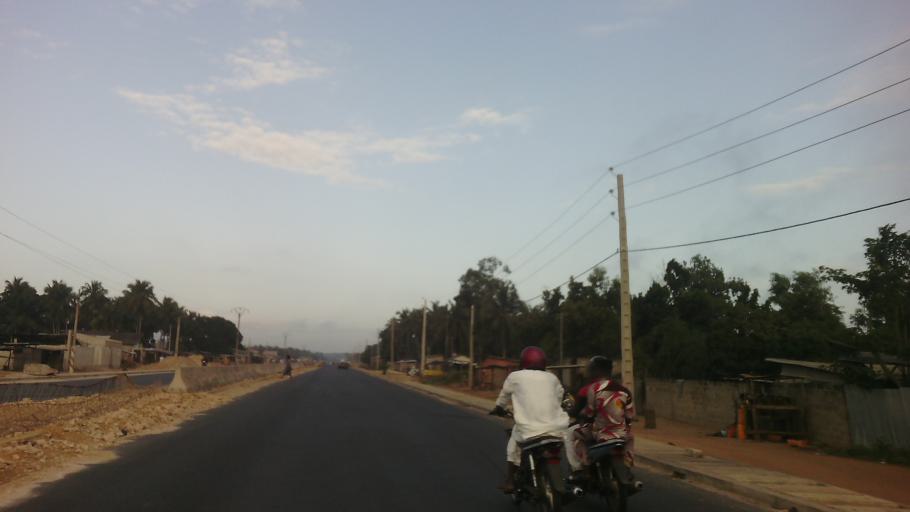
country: BJ
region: Atlantique
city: Hevie
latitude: 6.3836
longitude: 2.1891
